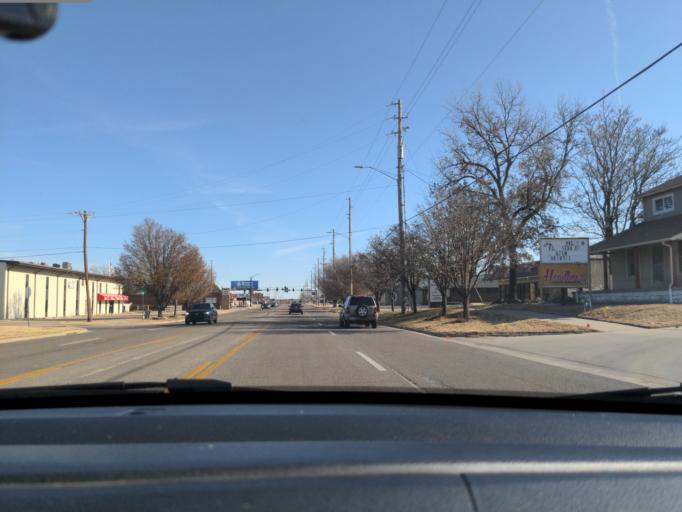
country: US
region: Kansas
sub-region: Sedgwick County
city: Wichita
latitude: 37.6948
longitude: -97.3828
